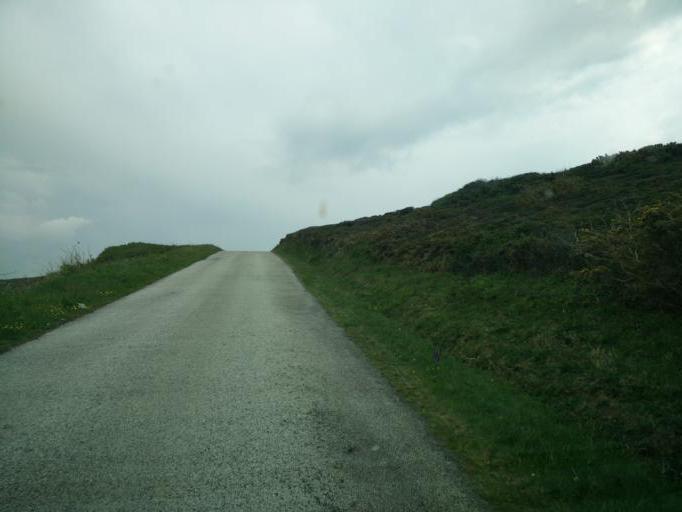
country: FR
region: Brittany
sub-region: Departement du Finistere
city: Roscanvel
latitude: 48.3056
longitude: -4.5690
